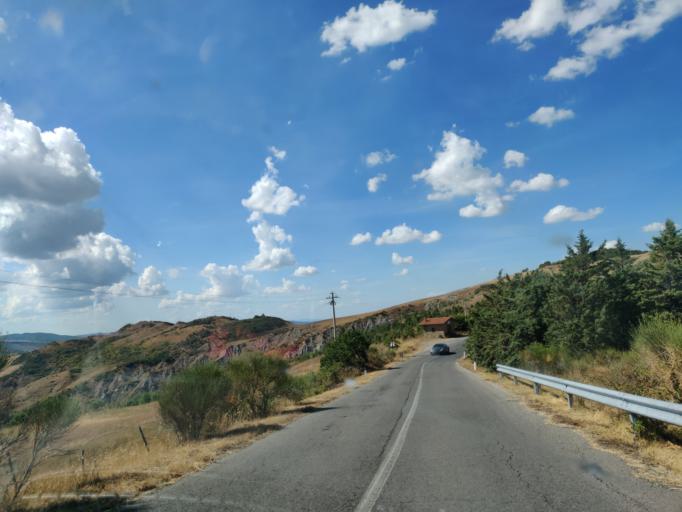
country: IT
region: Tuscany
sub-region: Provincia di Siena
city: Radicofani
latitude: 42.9422
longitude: 11.7349
